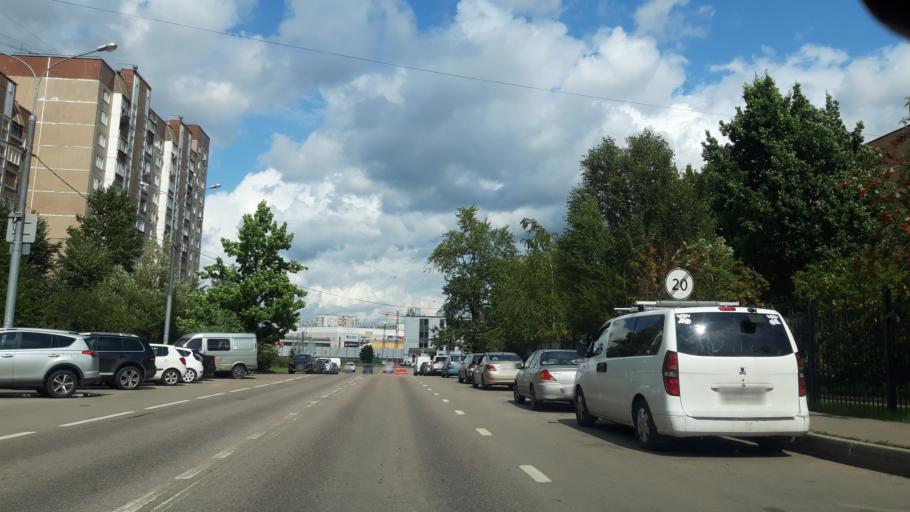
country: RU
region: Moscow
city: Zelenograd
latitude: 55.9798
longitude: 37.1680
